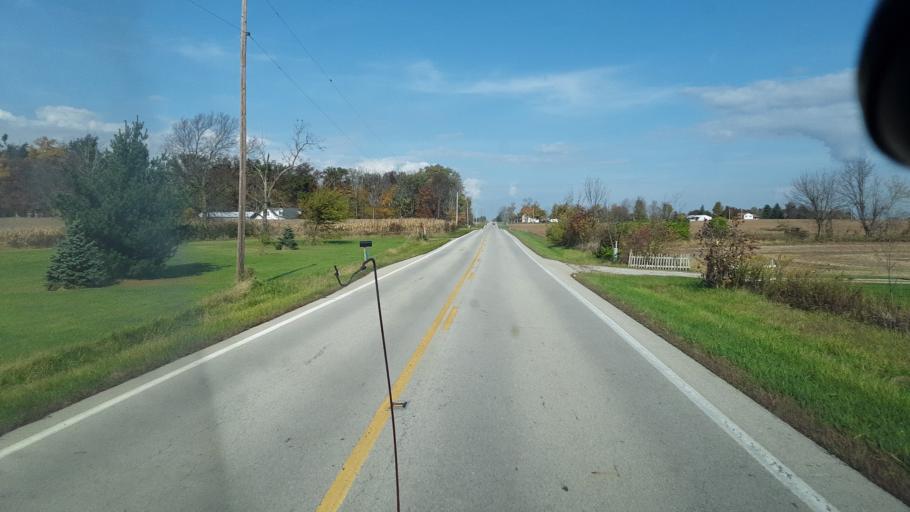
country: US
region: Ohio
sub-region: Clinton County
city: Sabina
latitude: 39.5147
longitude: -83.6915
